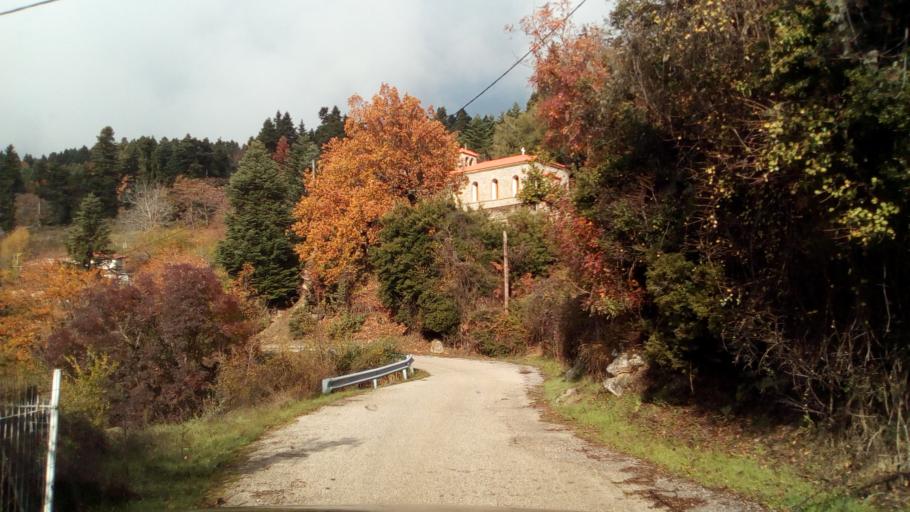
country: GR
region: West Greece
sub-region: Nomos Aitolias kai Akarnanias
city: Nafpaktos
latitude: 38.5674
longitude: 21.9206
